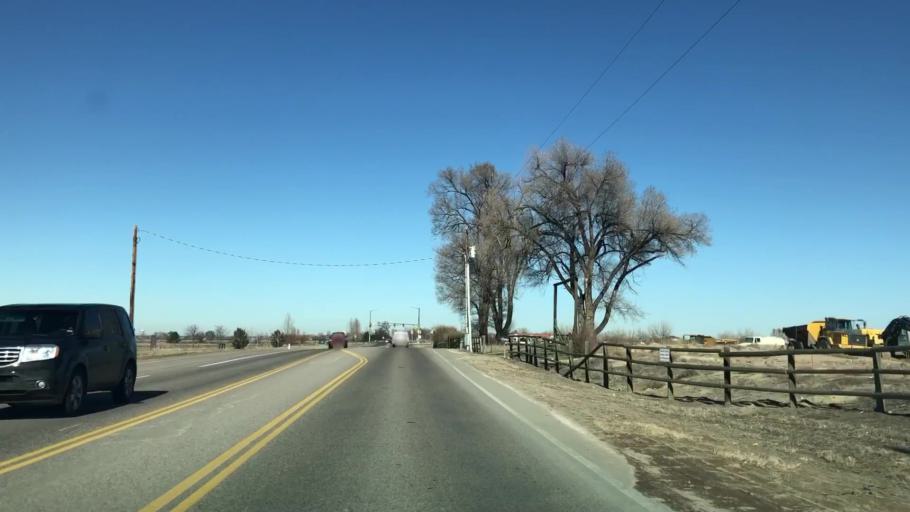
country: US
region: Colorado
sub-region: Weld County
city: Windsor
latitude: 40.4765
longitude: -104.9441
